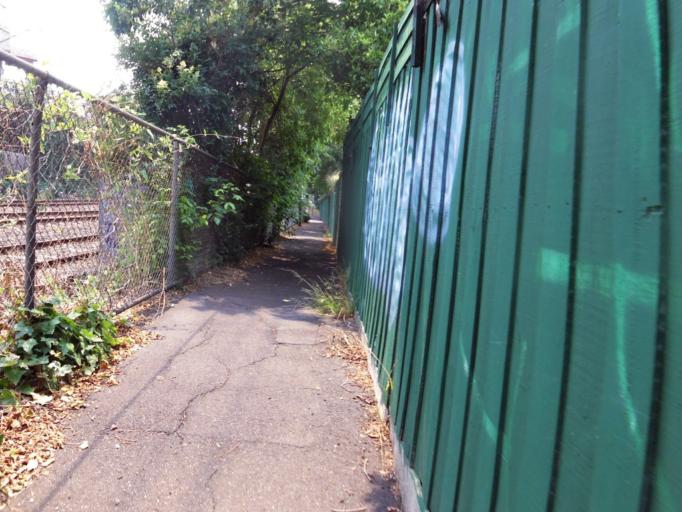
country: AU
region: Victoria
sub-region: Boroondara
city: Kew
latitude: -37.8233
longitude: 145.0214
